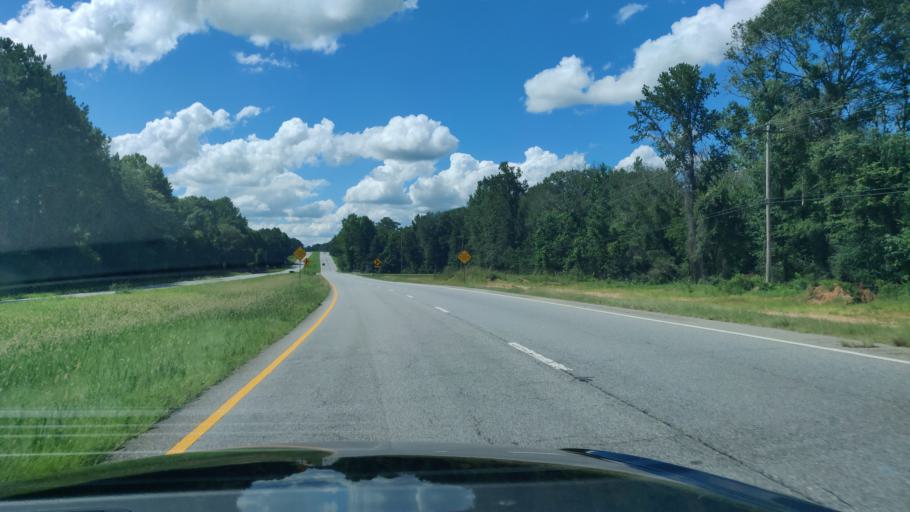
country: US
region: Georgia
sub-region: Chattahoochee County
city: Cusseta
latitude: 32.2814
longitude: -84.7593
